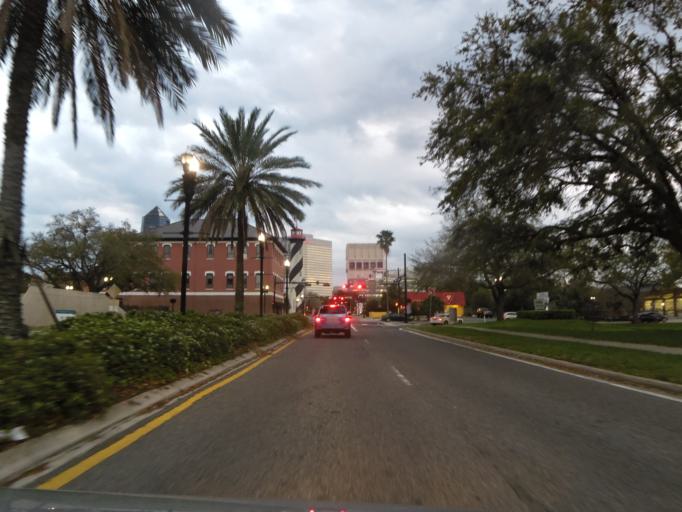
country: US
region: Florida
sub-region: Duval County
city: Jacksonville
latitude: 30.3347
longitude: -81.6609
